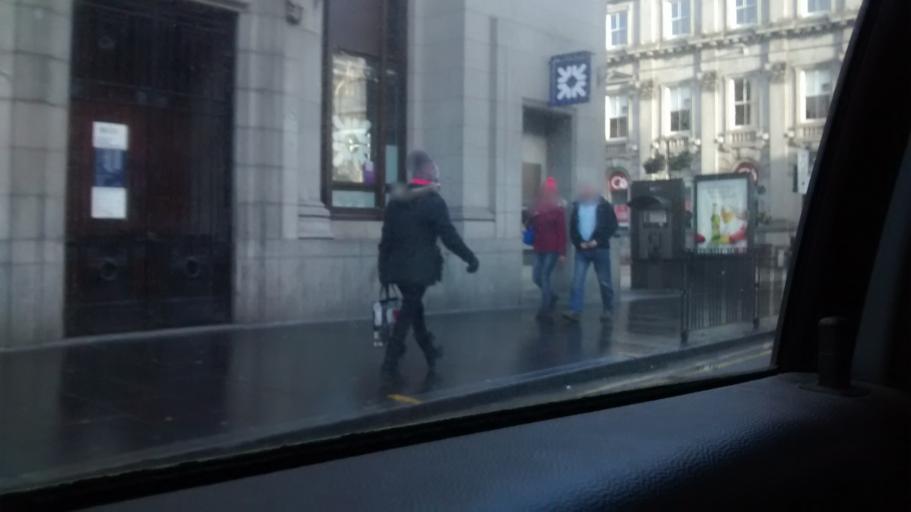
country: GB
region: Scotland
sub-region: Aberdeen City
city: Aberdeen
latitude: 57.1468
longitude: -2.0981
